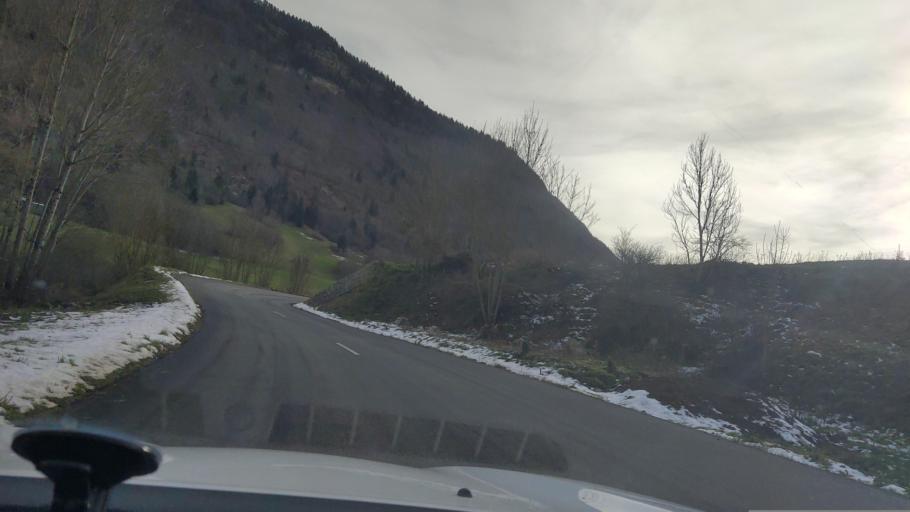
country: FR
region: Rhone-Alpes
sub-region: Departement de la Savoie
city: Coise-Saint-Jean-Pied-Gauthier
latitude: 45.6119
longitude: 6.1428
